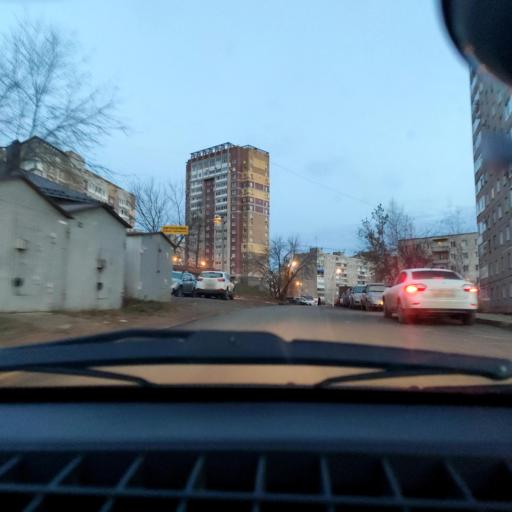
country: RU
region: Bashkortostan
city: Ufa
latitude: 54.7855
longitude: 56.0452
